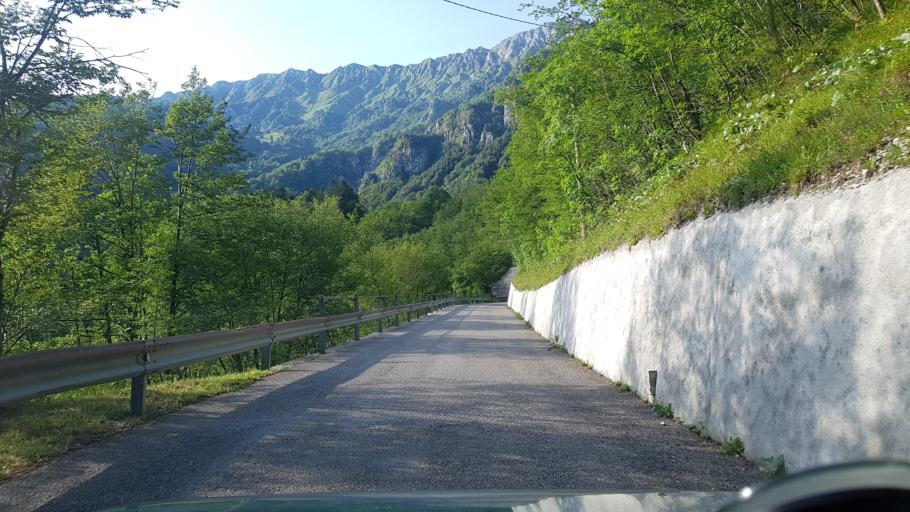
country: IT
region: Friuli Venezia Giulia
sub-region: Provincia di Udine
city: Lusevera
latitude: 46.3096
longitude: 13.2740
